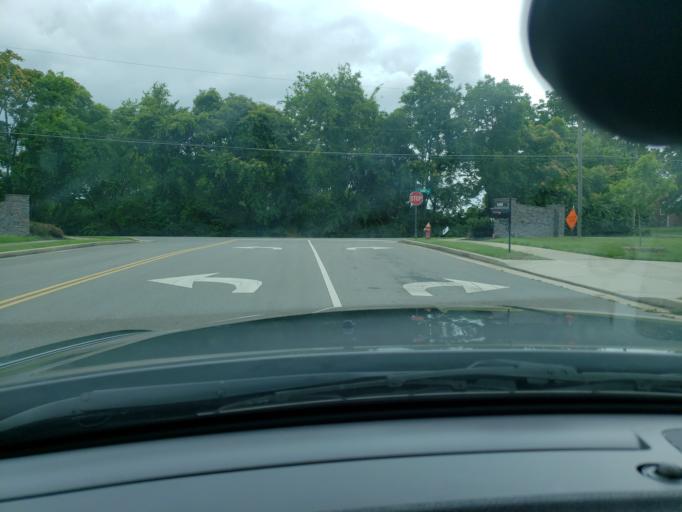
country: US
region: Tennessee
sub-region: Williamson County
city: Nolensville
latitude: 36.0251
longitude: -86.6905
